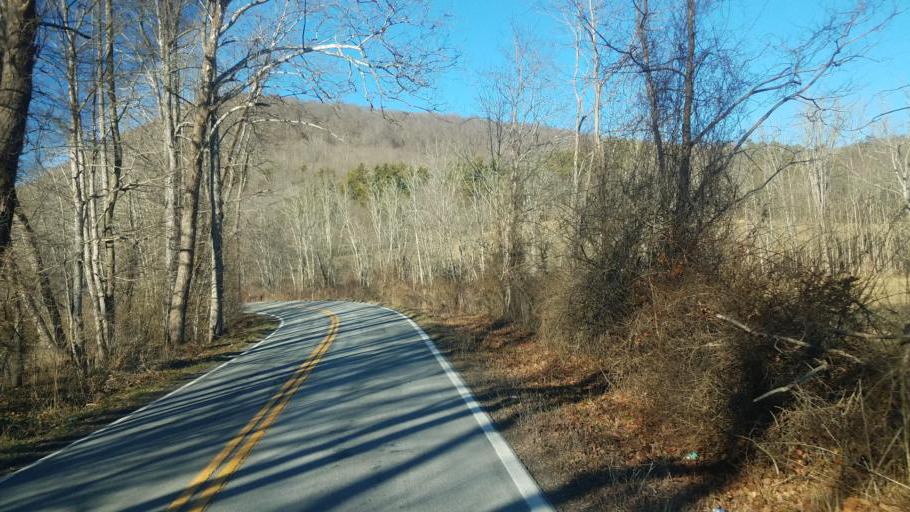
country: US
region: Virginia
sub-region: Pulaski County
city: Pulaski
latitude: 37.1680
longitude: -80.9012
